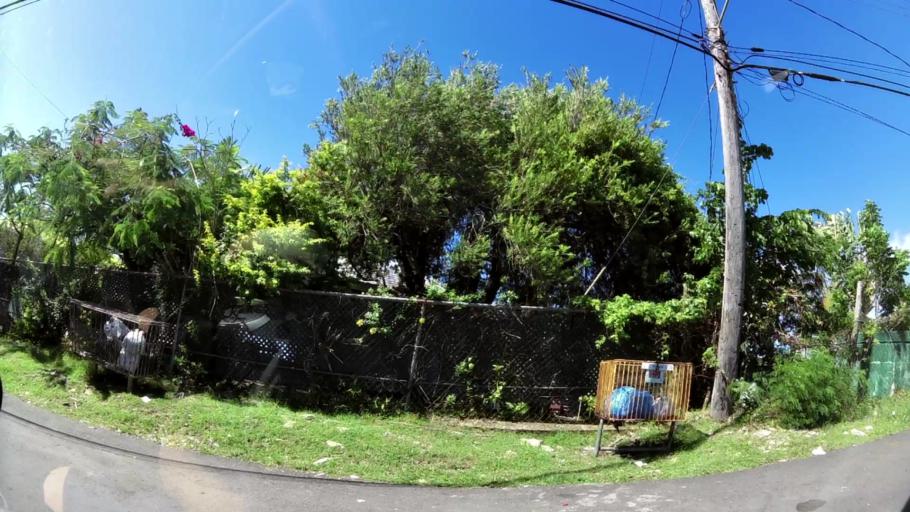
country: TT
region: Tobago
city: Scarborough
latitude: 11.1669
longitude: -60.7635
